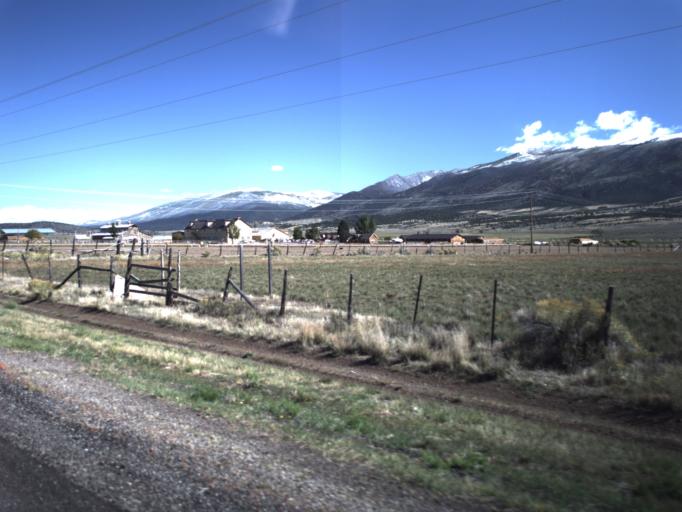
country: US
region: Utah
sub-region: Wayne County
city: Loa
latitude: 38.5139
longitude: -111.8814
